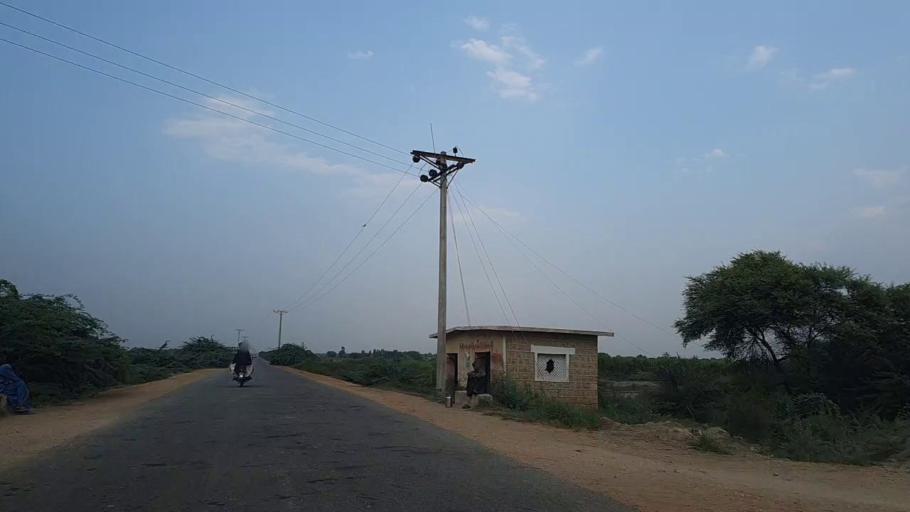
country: PK
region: Sindh
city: Daro Mehar
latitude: 24.7776
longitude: 68.1491
